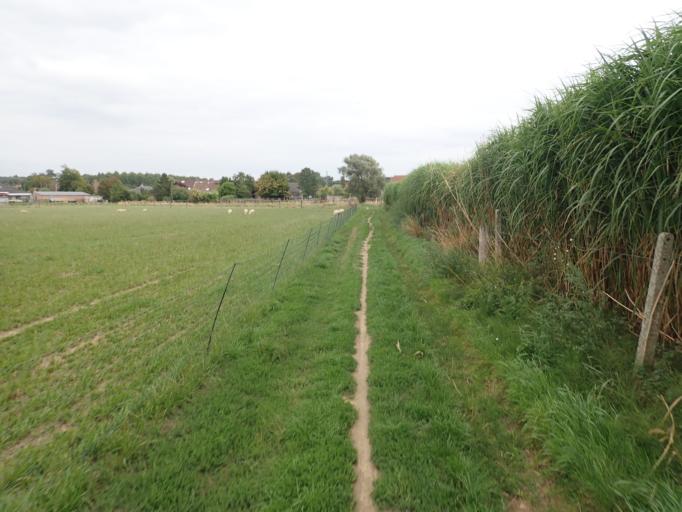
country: BE
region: Flanders
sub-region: Provincie Vlaams-Brabant
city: Asse
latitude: 50.9311
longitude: 4.2106
